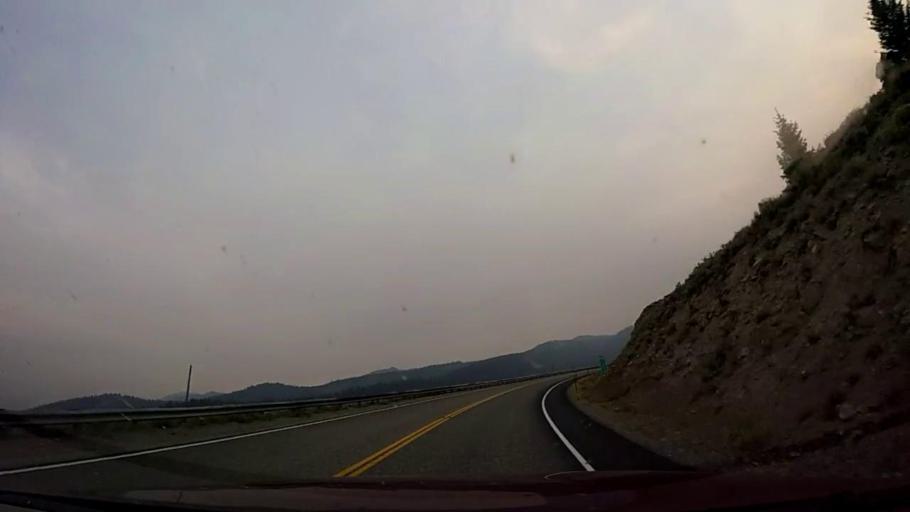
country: US
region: Idaho
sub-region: Blaine County
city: Ketchum
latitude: 43.8831
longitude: -114.6958
